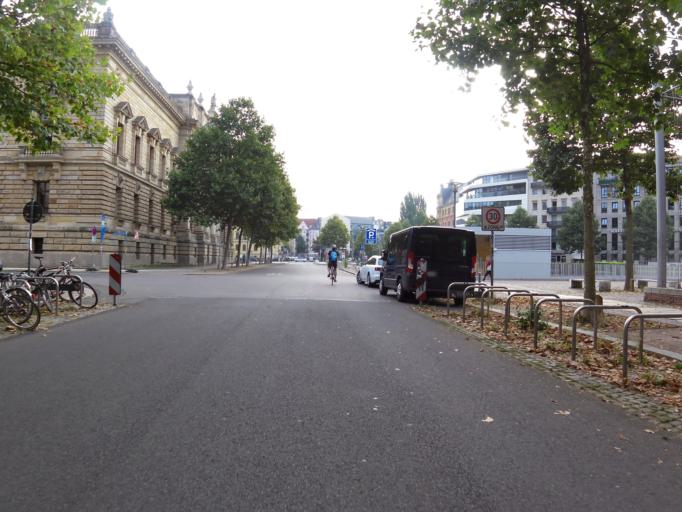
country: DE
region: Saxony
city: Leipzig
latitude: 51.3322
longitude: 12.3689
